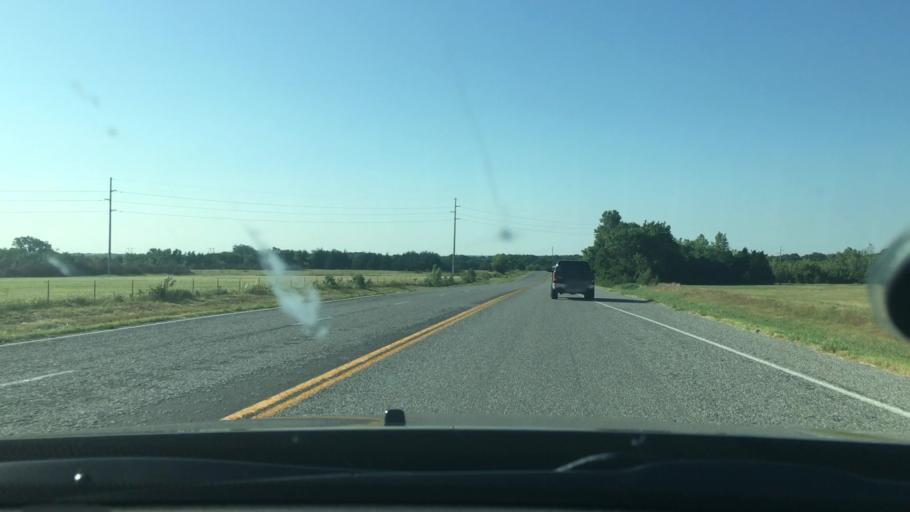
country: US
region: Oklahoma
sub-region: Johnston County
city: Tishomingo
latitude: 34.2765
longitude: -96.7777
